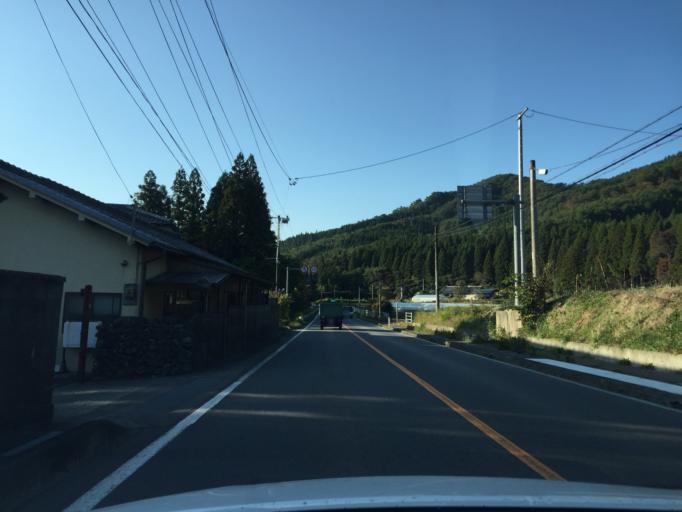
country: JP
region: Fukushima
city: Iwaki
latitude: 37.1138
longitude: 140.7561
